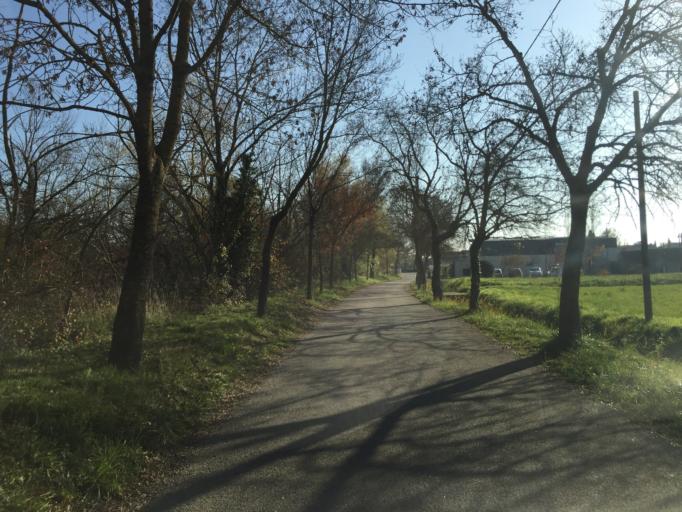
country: FR
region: Provence-Alpes-Cote d'Azur
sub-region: Departement du Vaucluse
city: Entraigues-sur-la-Sorgue
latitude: 44.0083
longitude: 4.9279
